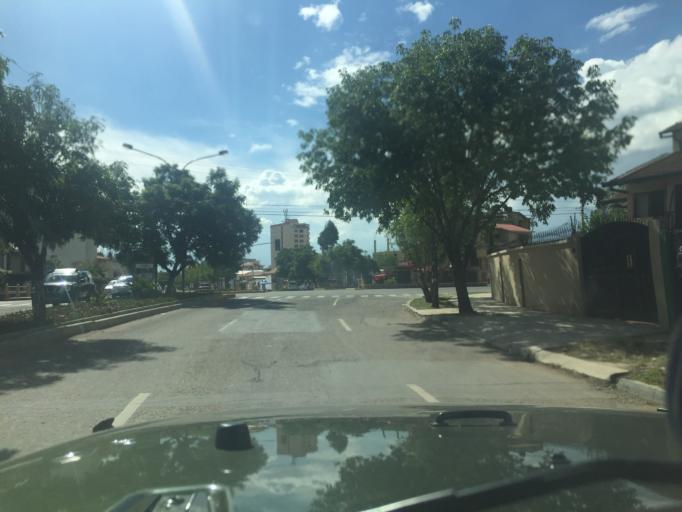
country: BO
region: Cochabamba
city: Cochabamba
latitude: -17.3775
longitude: -66.1684
